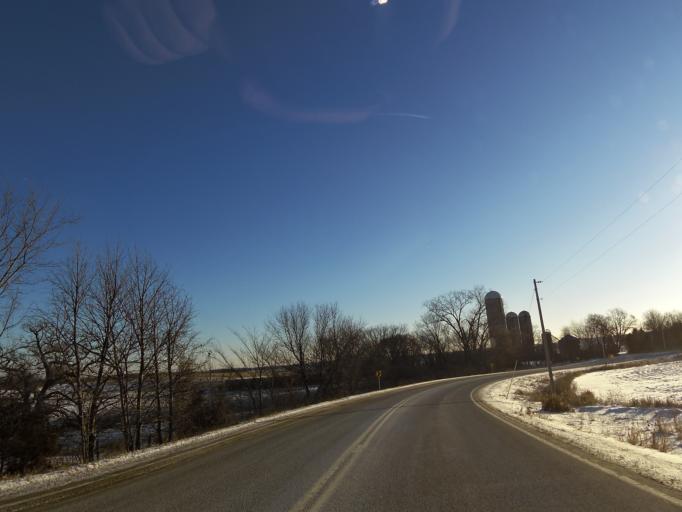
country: US
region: Minnesota
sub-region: Scott County
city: Jordan
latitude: 44.6633
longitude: -93.5342
